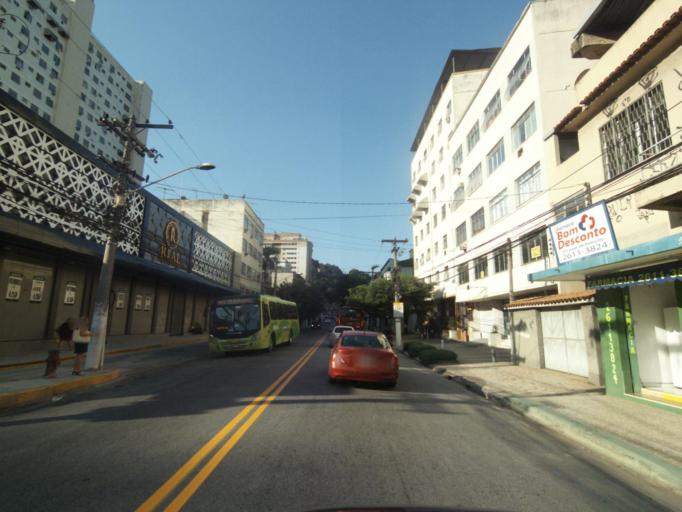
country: BR
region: Rio de Janeiro
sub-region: Niteroi
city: Niteroi
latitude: -22.8928
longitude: -43.0990
